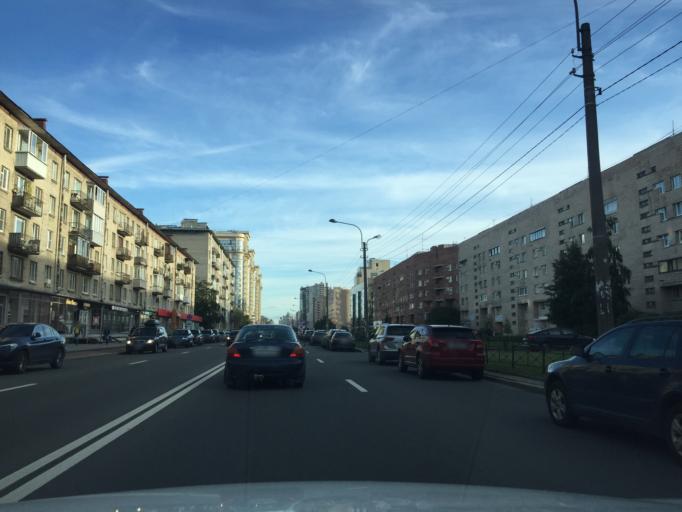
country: RU
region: St.-Petersburg
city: Kupchino
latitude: 59.8605
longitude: 30.3142
